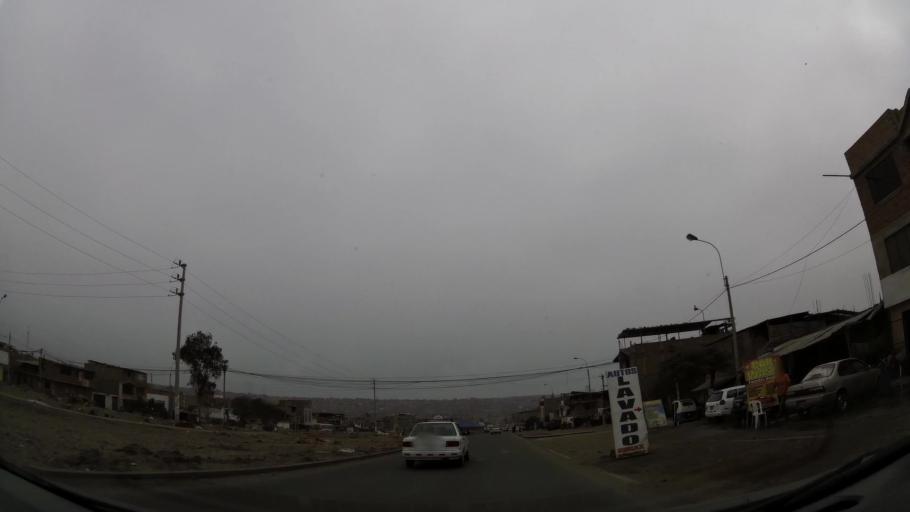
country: PE
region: Lima
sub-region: Lima
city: Surco
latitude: -12.2239
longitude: -76.9378
